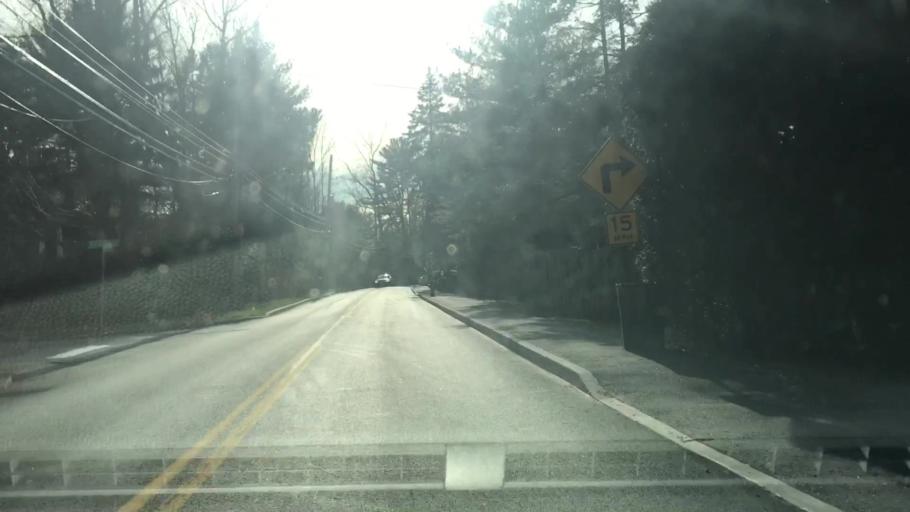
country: US
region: New York
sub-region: Westchester County
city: Greenville
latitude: 40.9901
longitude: -73.8284
